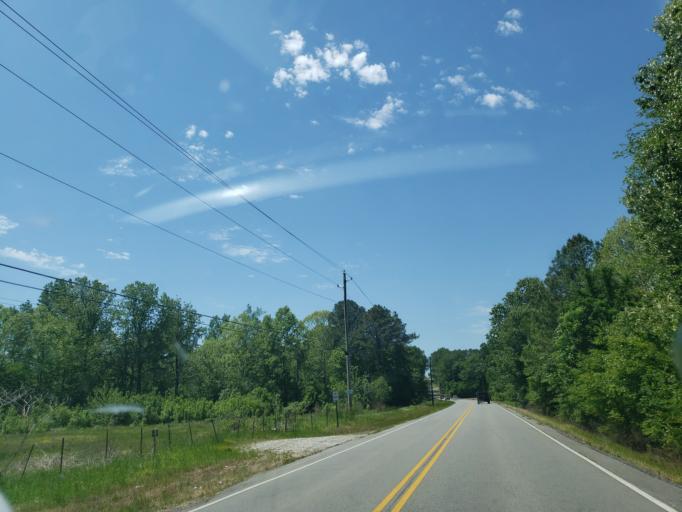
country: US
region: Alabama
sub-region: Madison County
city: Hazel Green
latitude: 34.9360
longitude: -86.5253
